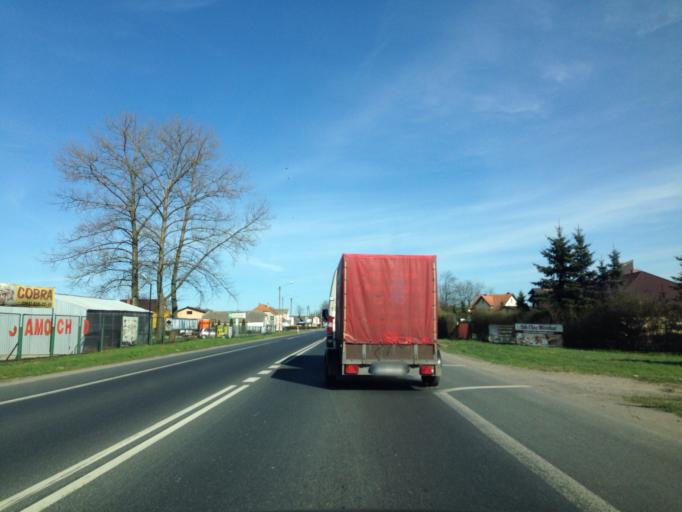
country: PL
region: Lodz Voivodeship
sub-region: Powiat sieradzki
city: Sieradz
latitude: 51.6011
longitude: 18.7843
